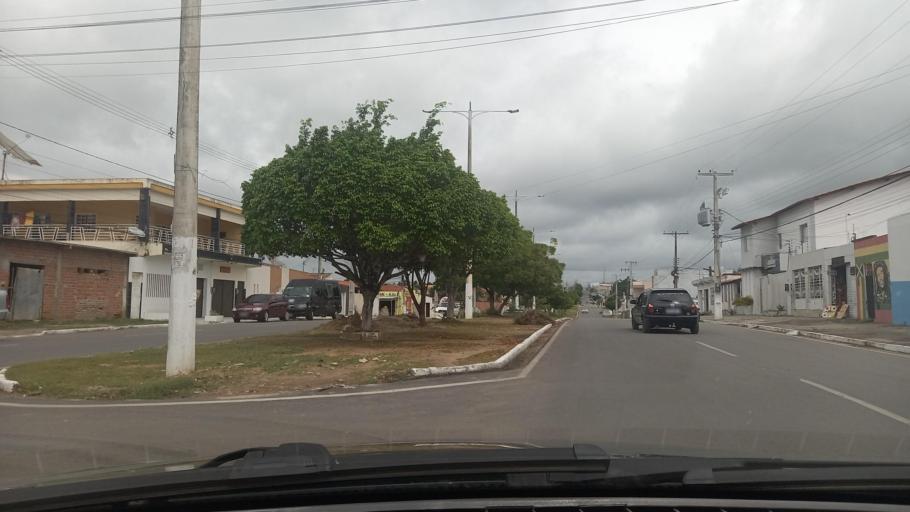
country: BR
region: Alagoas
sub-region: Delmiro Gouveia
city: Delmiro Gouveia
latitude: -9.3825
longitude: -38.0066
